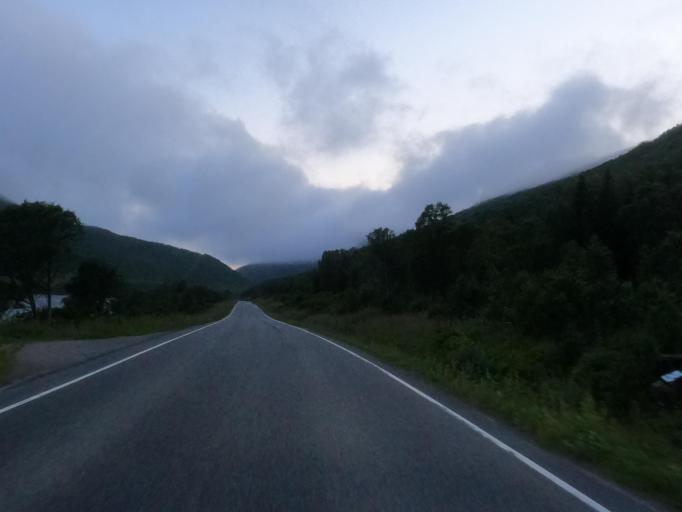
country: NO
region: Nordland
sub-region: Sortland
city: Sortland
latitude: 68.6201
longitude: 15.7081
